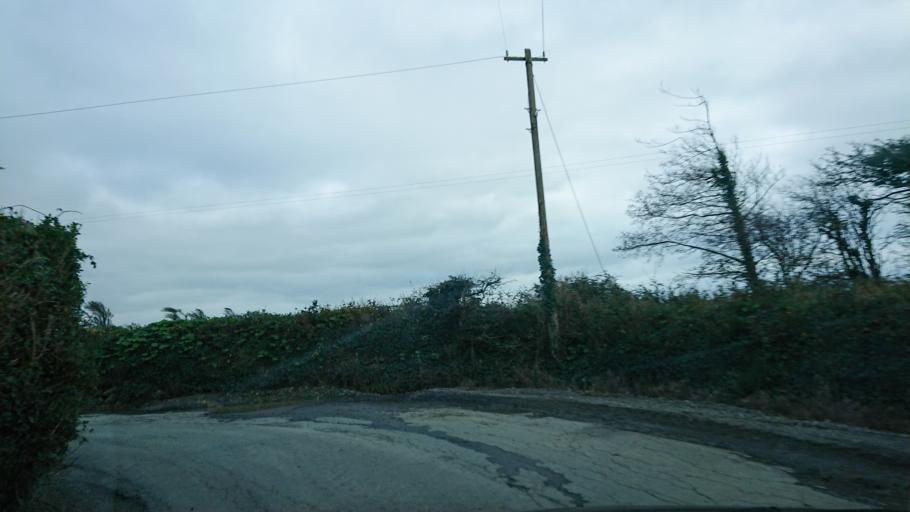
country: IE
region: Munster
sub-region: Waterford
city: Dunmore East
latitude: 52.1775
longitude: -7.0462
